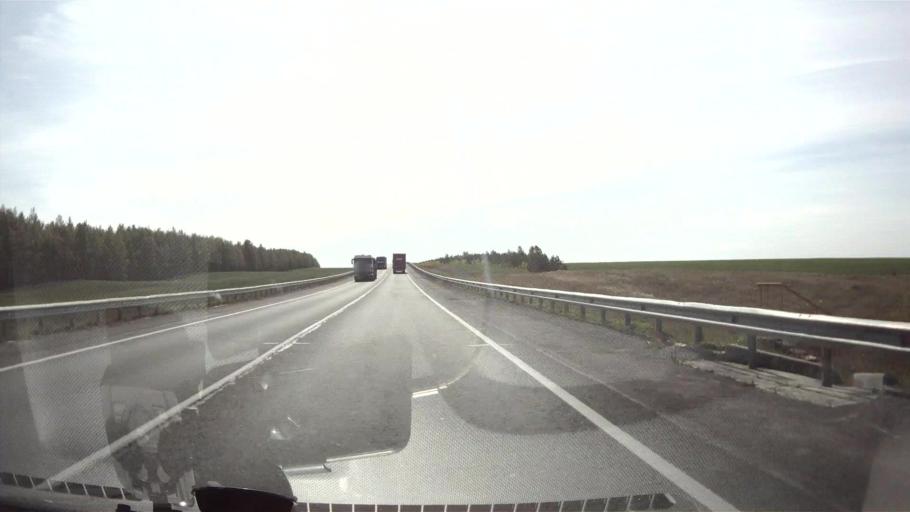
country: RU
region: Samara
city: Syzran'
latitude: 52.9003
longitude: 48.2963
